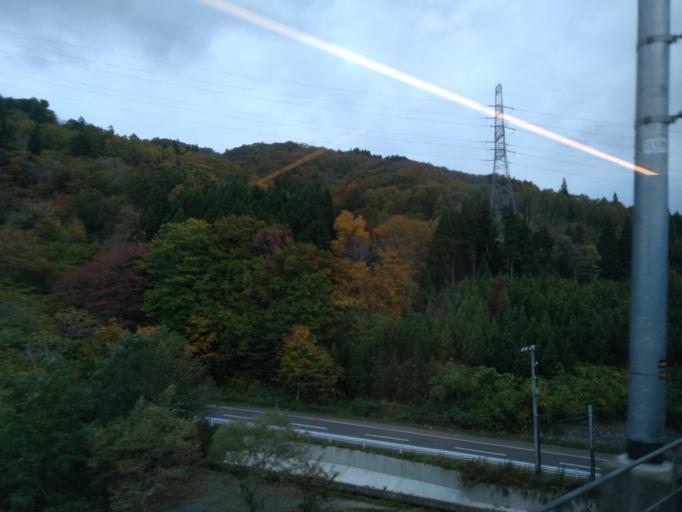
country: JP
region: Aomori
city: Goshogawara
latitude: 41.1512
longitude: 140.5101
